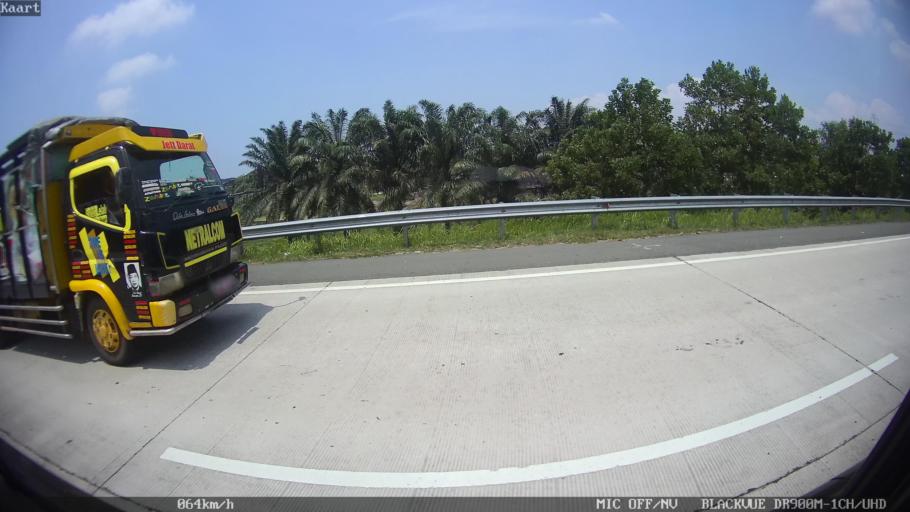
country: ID
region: Lampung
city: Kedaton
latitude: -5.3472
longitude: 105.3194
